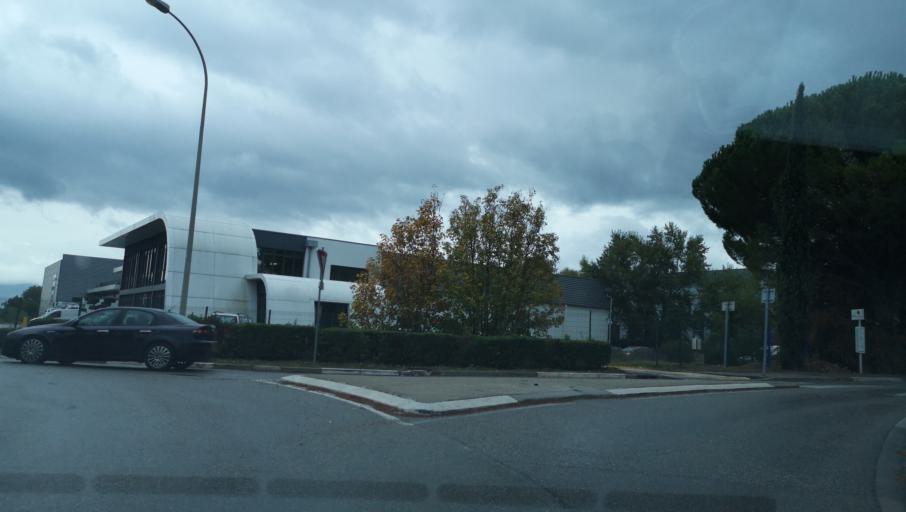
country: FR
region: Provence-Alpes-Cote d'Azur
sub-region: Departement des Bouches-du-Rhone
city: Rousset
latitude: 43.4681
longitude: 5.6132
